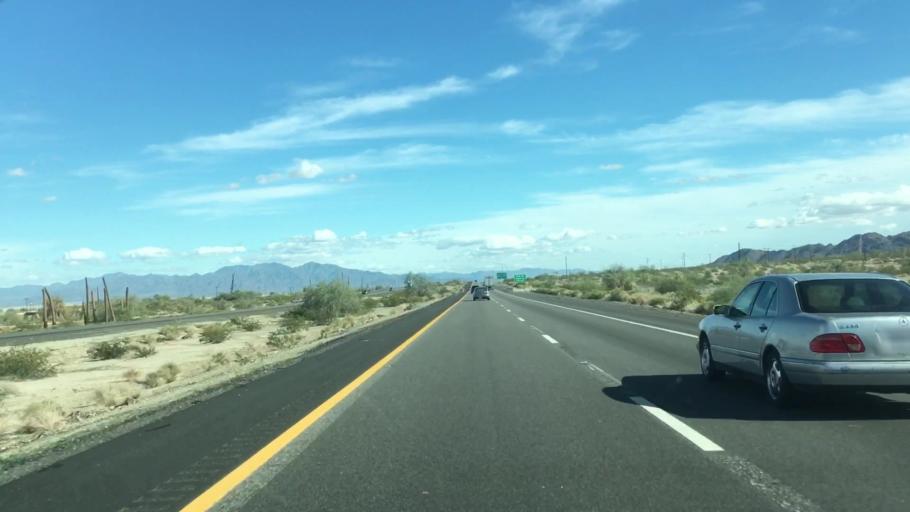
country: US
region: California
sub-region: Imperial County
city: Niland
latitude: 33.7102
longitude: -115.4093
